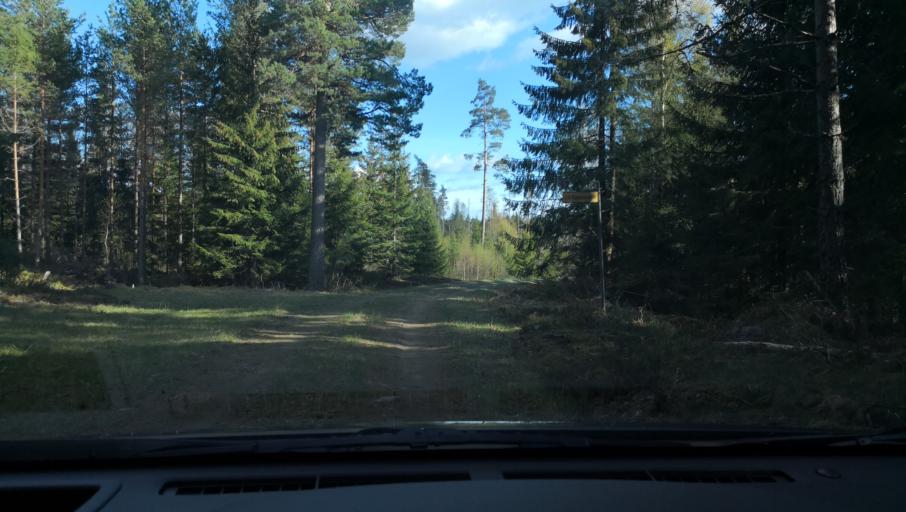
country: SE
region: OErebro
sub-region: Askersunds Kommun
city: Asbro
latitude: 58.8700
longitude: 15.1270
